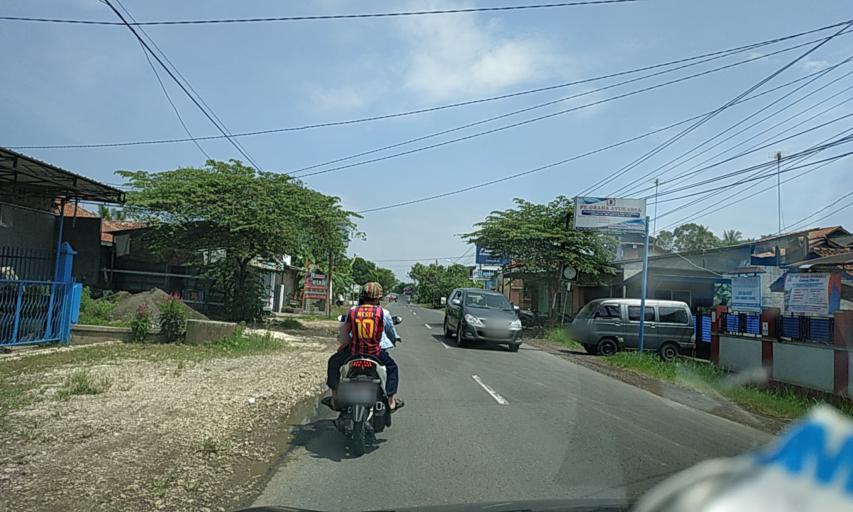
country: ID
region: Central Java
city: Tambangan
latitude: -7.4865
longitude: 108.8171
